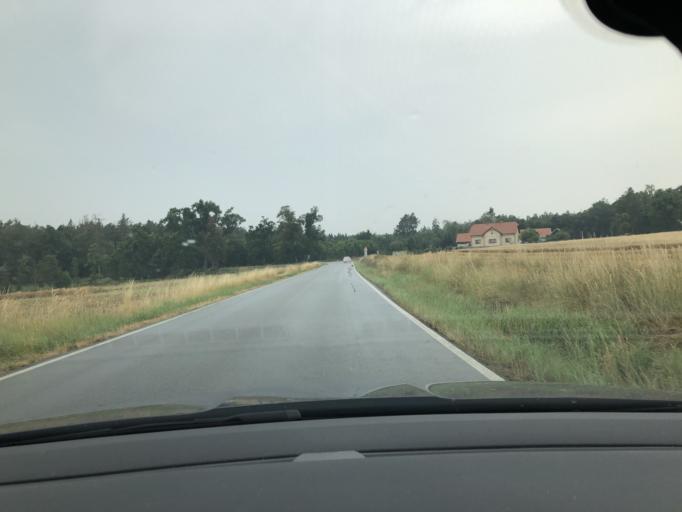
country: CZ
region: South Moravian
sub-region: Okres Znojmo
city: Jevisovice
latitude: 49.0294
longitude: 15.9616
